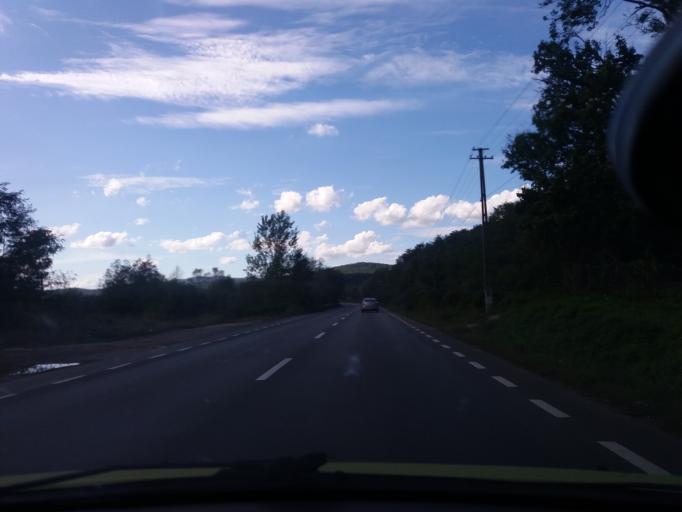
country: RO
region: Arad
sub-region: Comuna Conop
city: Conop
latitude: 46.1032
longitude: 21.8722
